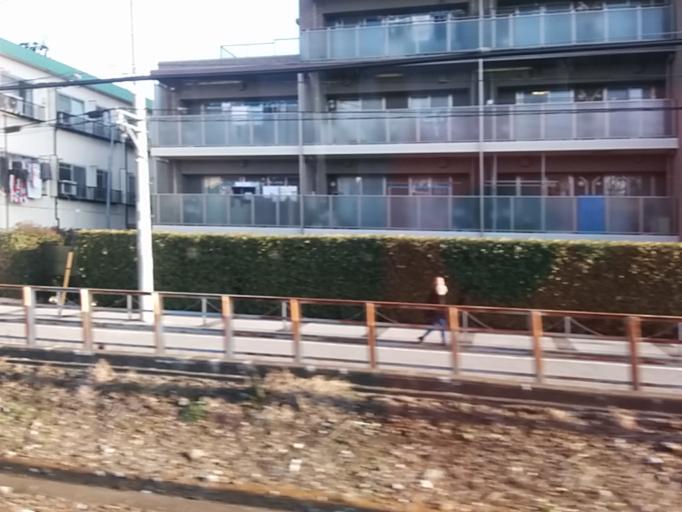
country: JP
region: Saitama
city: Wako
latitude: 35.7799
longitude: 139.6296
